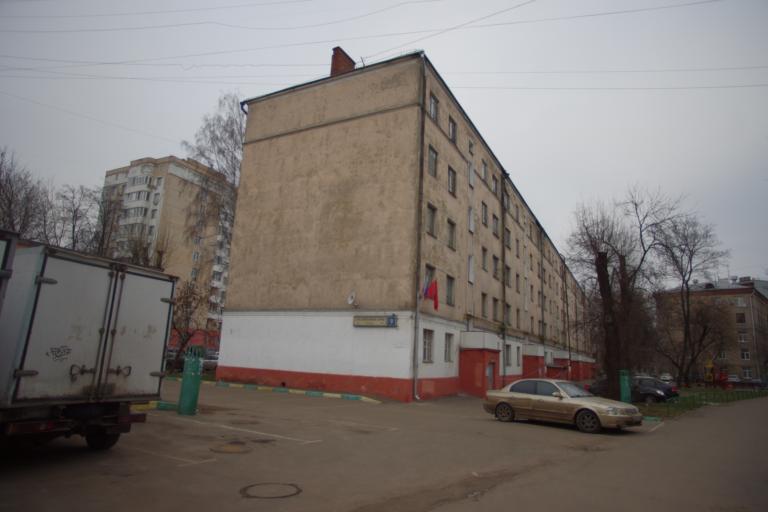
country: RU
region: Moscow
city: Lefortovo
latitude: 55.7719
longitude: 37.7330
